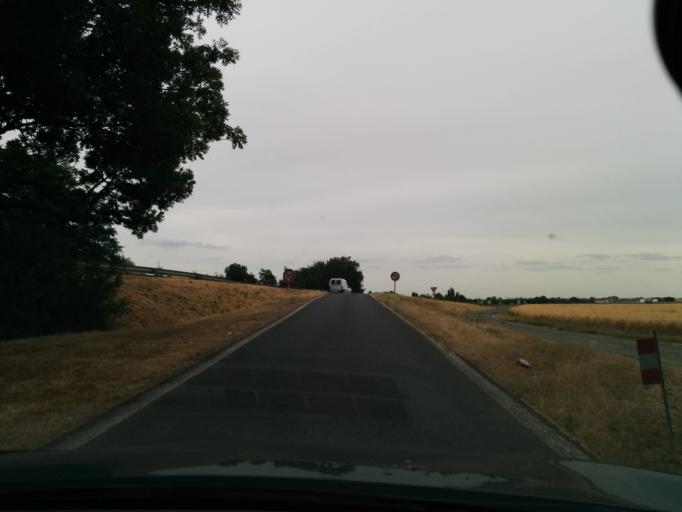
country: FR
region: Ile-de-France
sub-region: Departement de l'Essonne
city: Angerville
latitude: 48.3082
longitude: 1.9923
